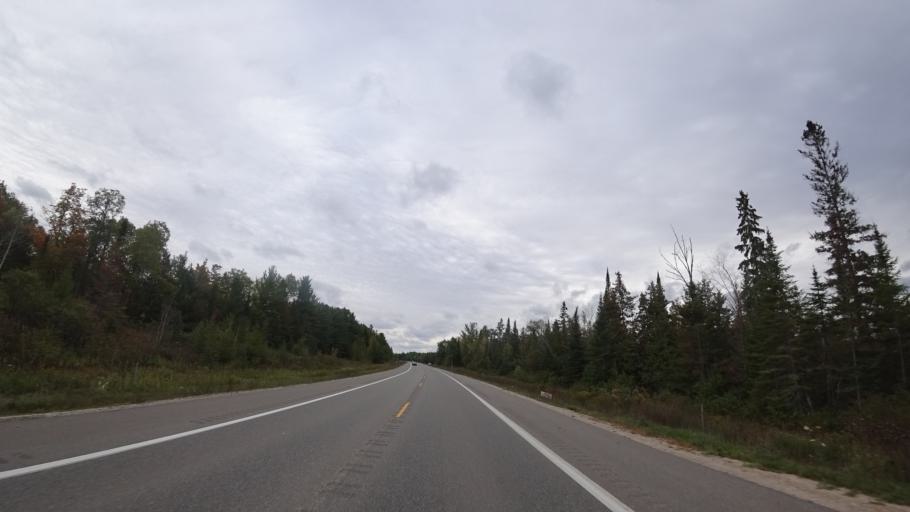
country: US
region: Michigan
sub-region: Charlevoix County
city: Boyne City
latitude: 45.1551
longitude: -84.9194
